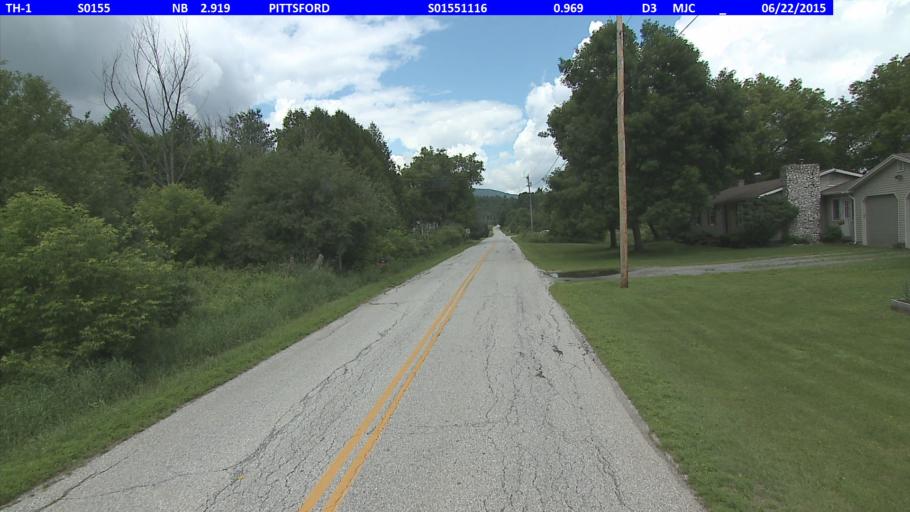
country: US
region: Vermont
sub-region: Rutland County
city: Brandon
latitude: 43.7049
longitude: -73.0483
